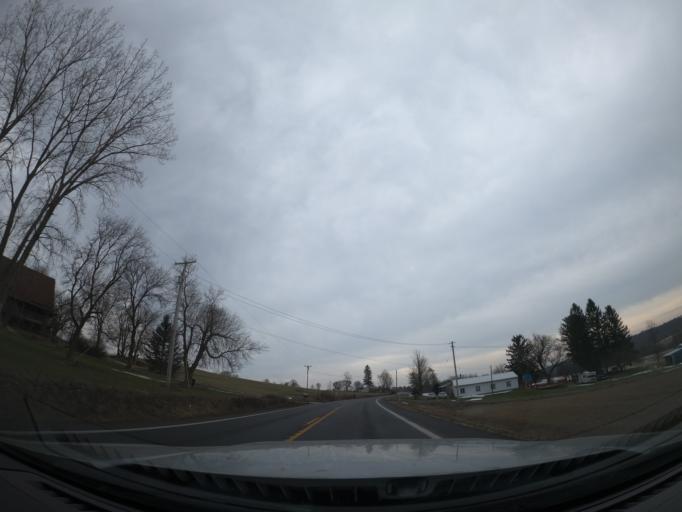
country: US
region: New York
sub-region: Cayuga County
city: Moravia
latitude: 42.7125
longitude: -76.5433
